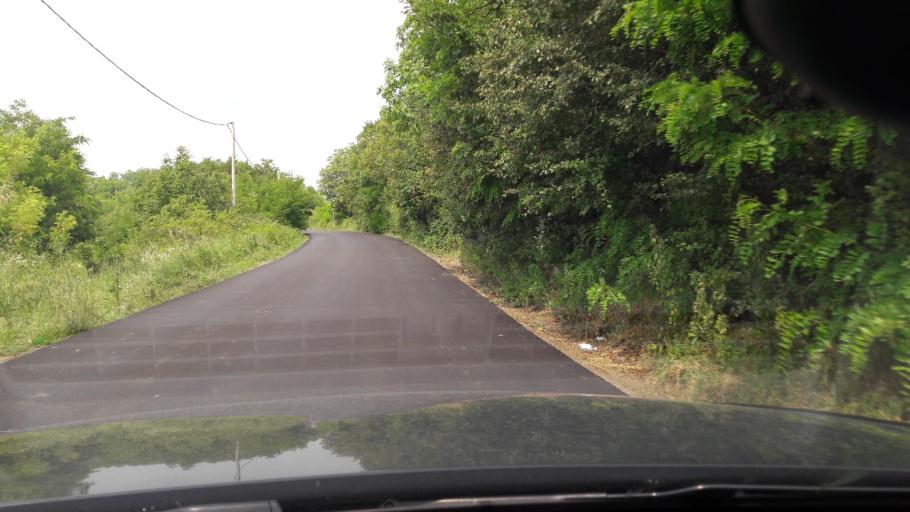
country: RS
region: Central Serbia
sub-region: Belgrade
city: Sopot
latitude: 44.6045
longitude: 20.6011
